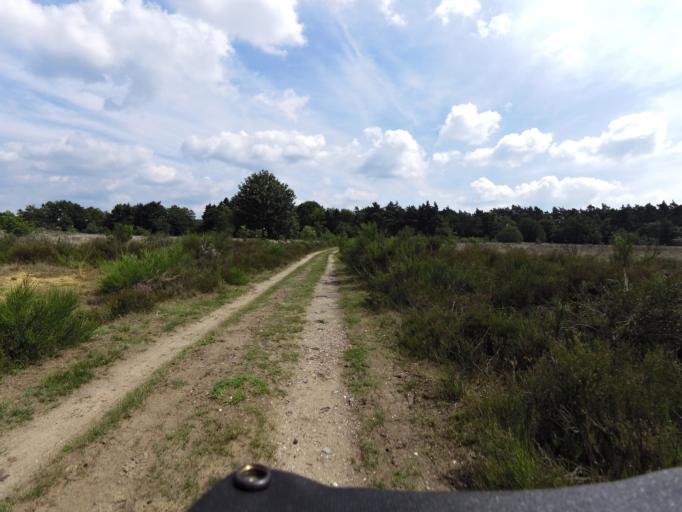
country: NL
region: Limburg
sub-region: Gemeente Roerdalen
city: Vlodrop
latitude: 51.1745
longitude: 6.1364
